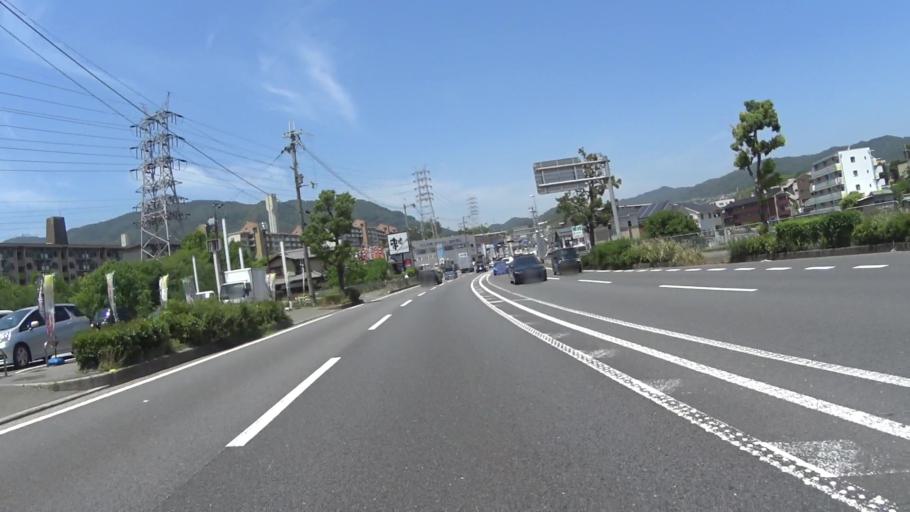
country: JP
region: Kyoto
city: Muko
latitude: 34.9706
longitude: 135.6762
